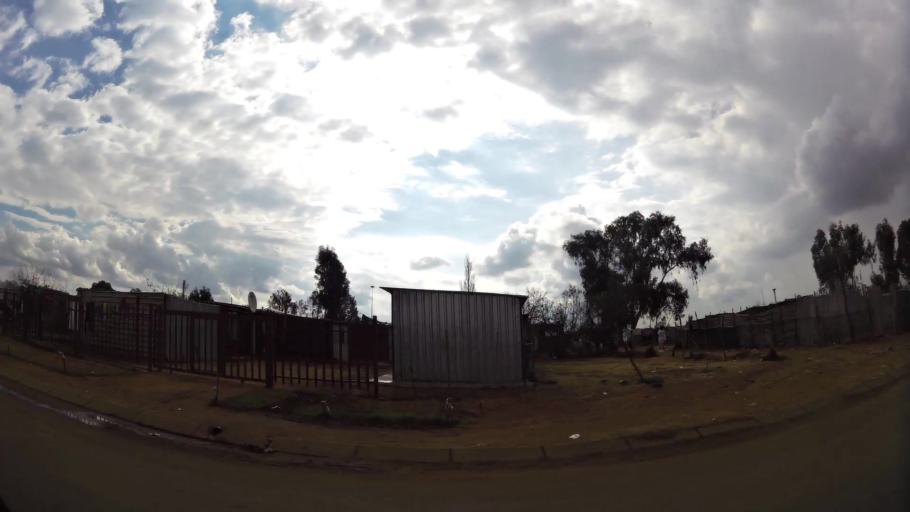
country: ZA
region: Gauteng
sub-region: Sedibeng District Municipality
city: Vanderbijlpark
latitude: -26.6979
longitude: 27.7994
